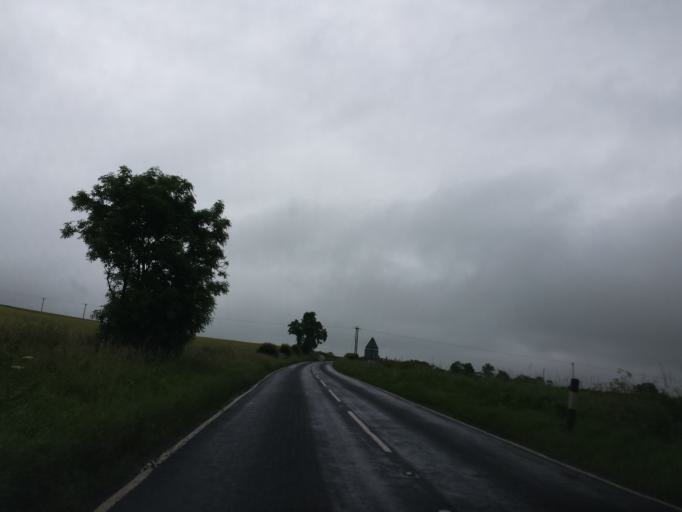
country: GB
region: Scotland
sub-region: Fife
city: Lundin Links
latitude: 56.2305
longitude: -2.9036
